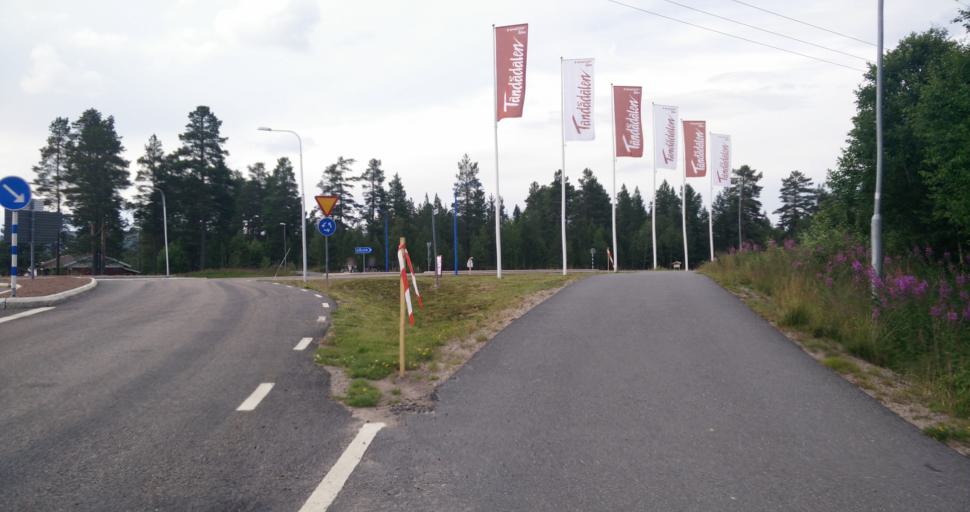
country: NO
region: Hedmark
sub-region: Trysil
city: Innbygda
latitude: 61.1794
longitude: 12.9926
